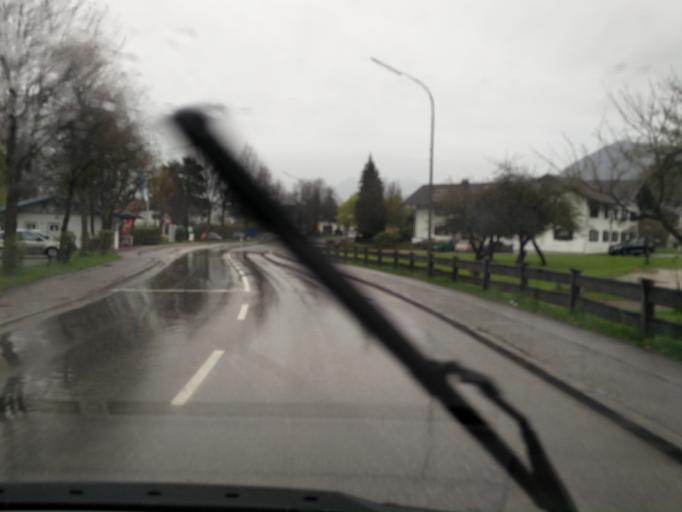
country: DE
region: Bavaria
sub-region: Upper Bavaria
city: Bernau am Chiemsee
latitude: 47.8112
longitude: 12.3745
